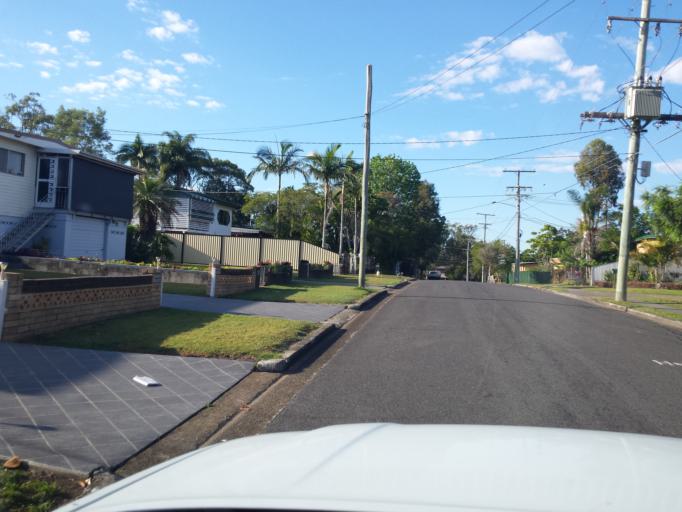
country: AU
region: Queensland
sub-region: Logan
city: Logan City
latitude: -27.6484
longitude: 153.1116
